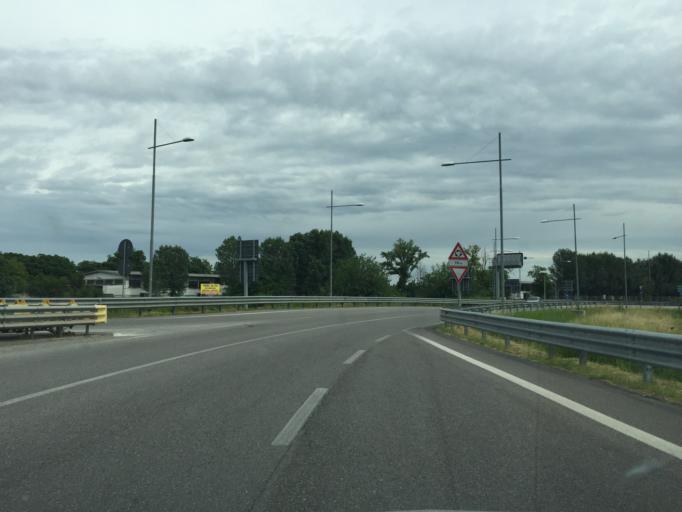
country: IT
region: Lombardy
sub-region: Provincia di Brescia
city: Borgosatollo
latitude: 45.4596
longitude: 10.2449
